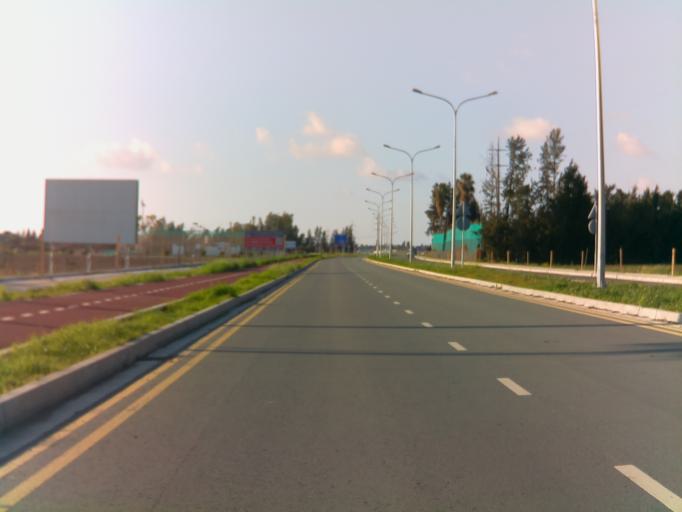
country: CY
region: Pafos
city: Paphos
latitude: 34.7408
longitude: 32.4498
